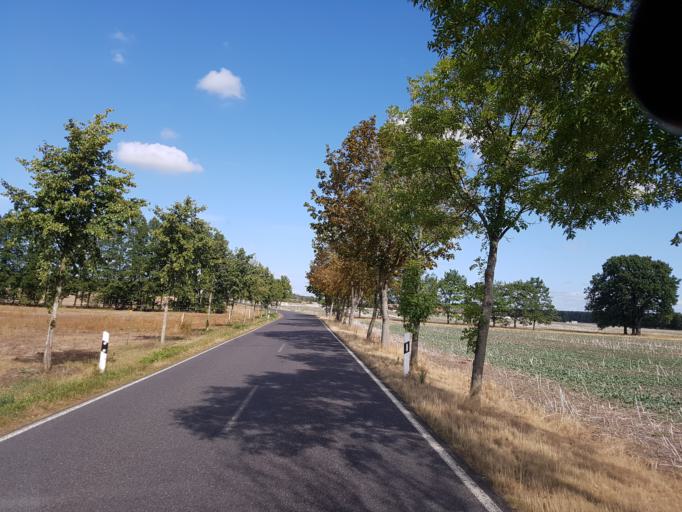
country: DE
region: Brandenburg
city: Sonnewalde
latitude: 51.7484
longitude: 13.6170
